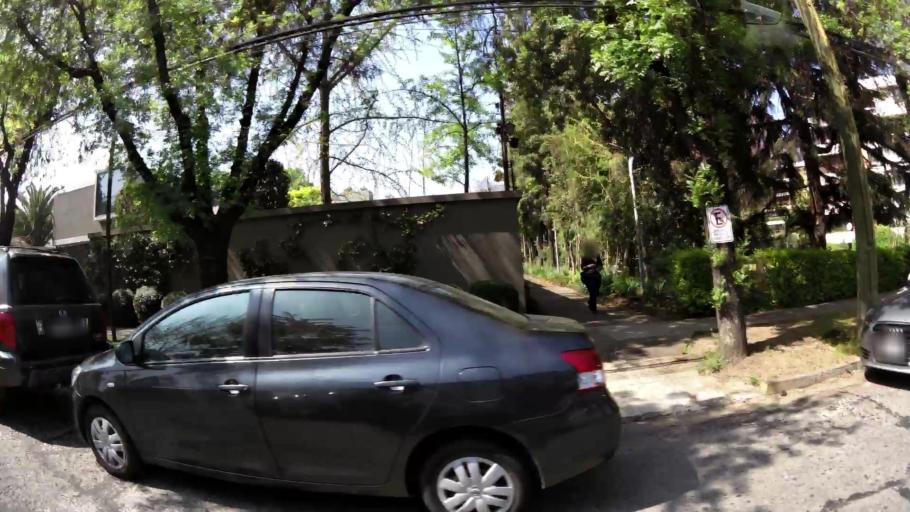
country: CL
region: Santiago Metropolitan
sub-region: Provincia de Santiago
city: Villa Presidente Frei, Nunoa, Santiago, Chile
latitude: -33.3906
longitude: -70.5823
